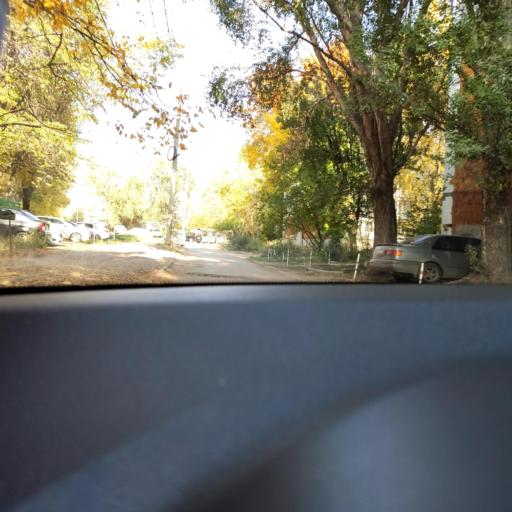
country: RU
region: Samara
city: Petra-Dubrava
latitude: 53.2445
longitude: 50.2620
